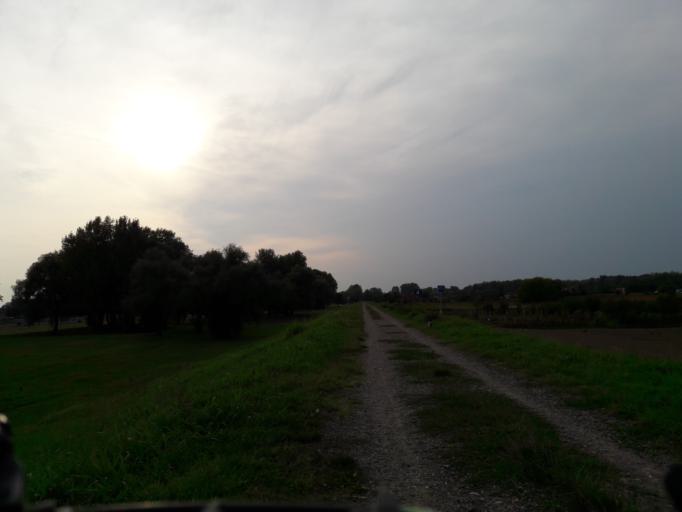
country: HR
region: Osjecko-Baranjska
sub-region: Grad Osijek
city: Osijek
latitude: 45.5665
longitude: 18.6809
